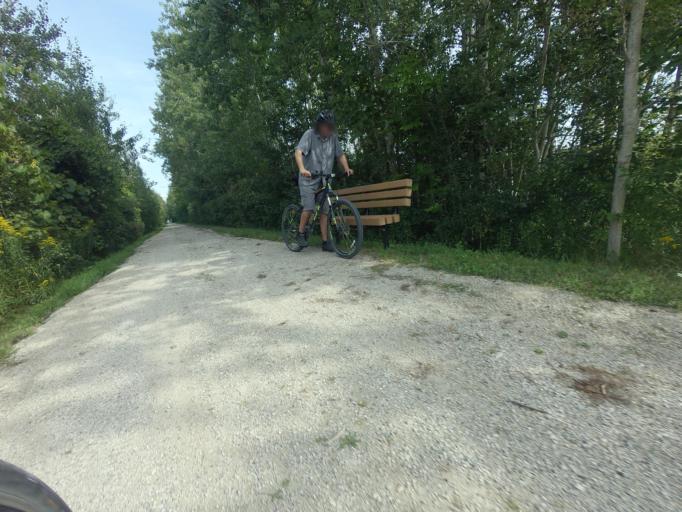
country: CA
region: Ontario
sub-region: Wellington County
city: Guelph
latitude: 43.5789
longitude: -80.3868
